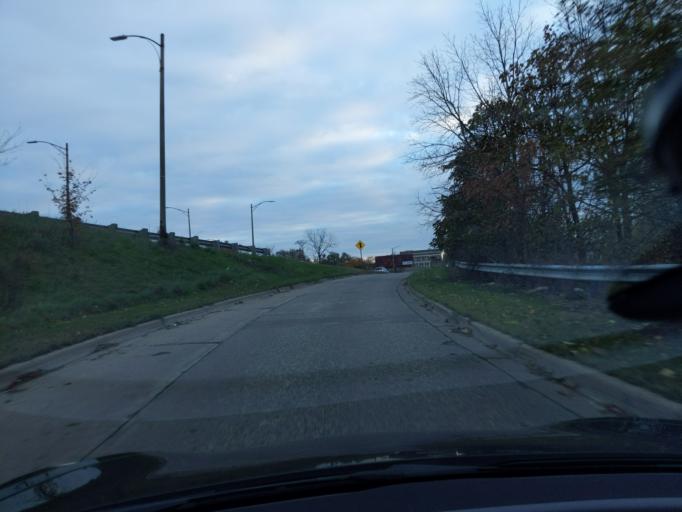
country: US
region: Michigan
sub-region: Ingham County
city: Lansing
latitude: 42.7506
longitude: -84.5460
